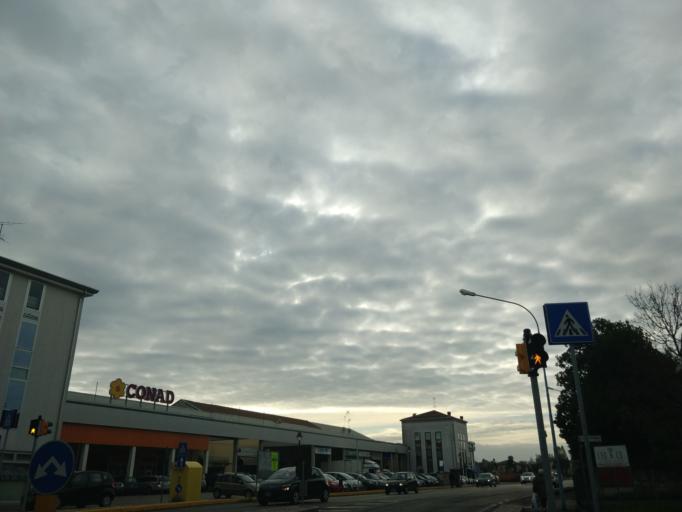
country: IT
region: Emilia-Romagna
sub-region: Provincia di Bologna
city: Pieve di Cento
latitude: 44.7110
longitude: 11.3060
